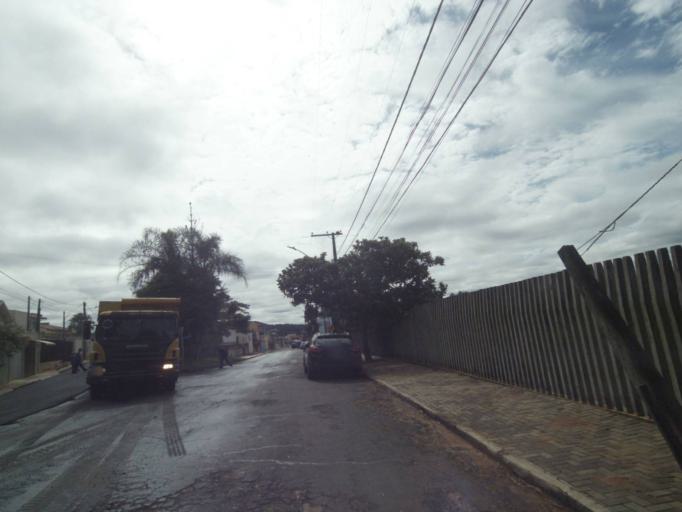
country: BR
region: Parana
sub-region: Telemaco Borba
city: Telemaco Borba
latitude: -24.3338
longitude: -50.6225
